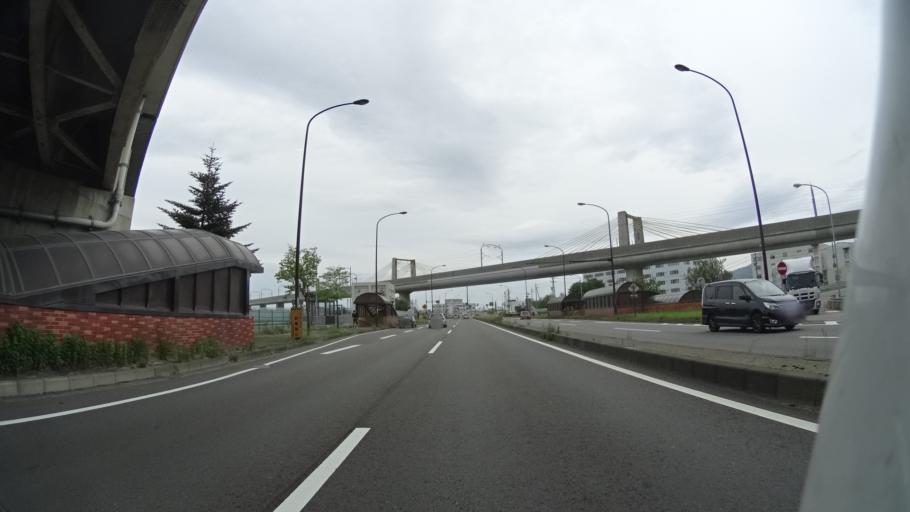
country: JP
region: Nagano
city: Nagano-shi
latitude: 36.5469
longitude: 138.1293
